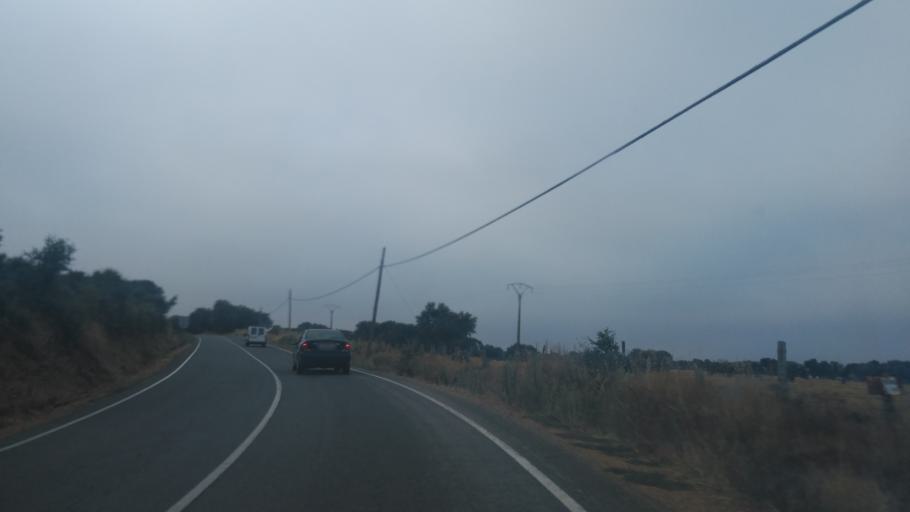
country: ES
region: Castille and Leon
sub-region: Provincia de Salamanca
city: Robliza de Cojos
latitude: 40.8509
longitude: -5.9595
